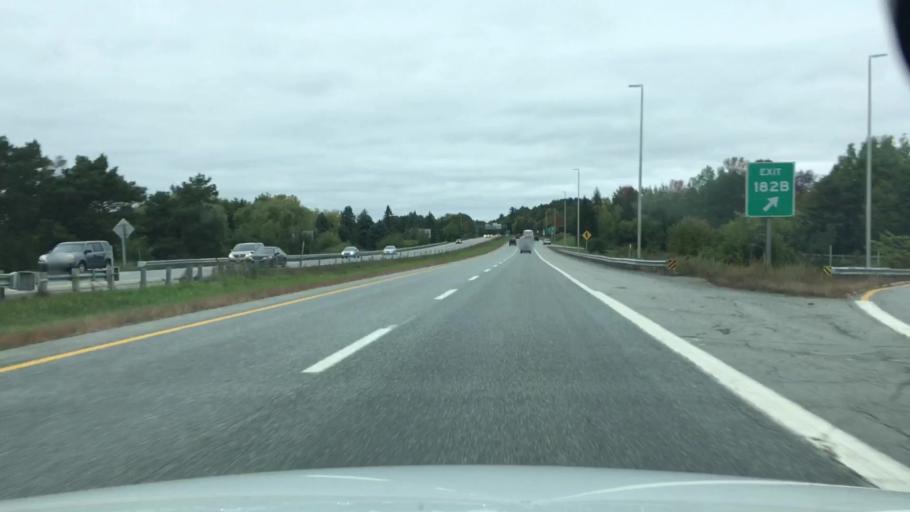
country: US
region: Maine
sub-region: Penobscot County
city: Bangor
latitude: 44.7881
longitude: -68.8074
